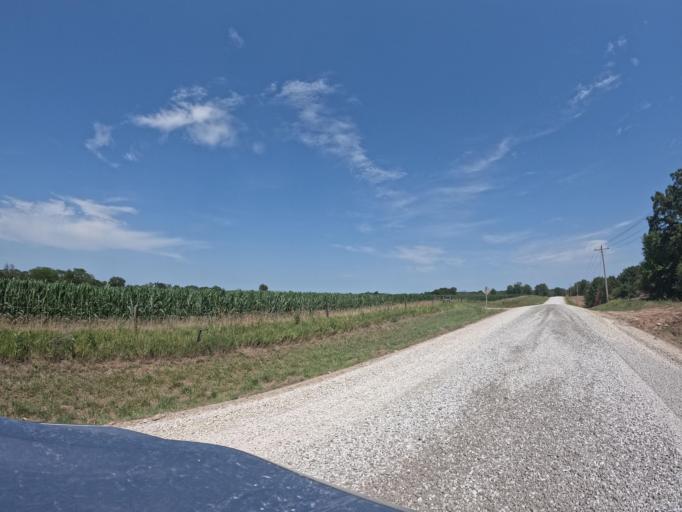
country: US
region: Iowa
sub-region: Henry County
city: Mount Pleasant
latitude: 40.8934
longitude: -91.6941
